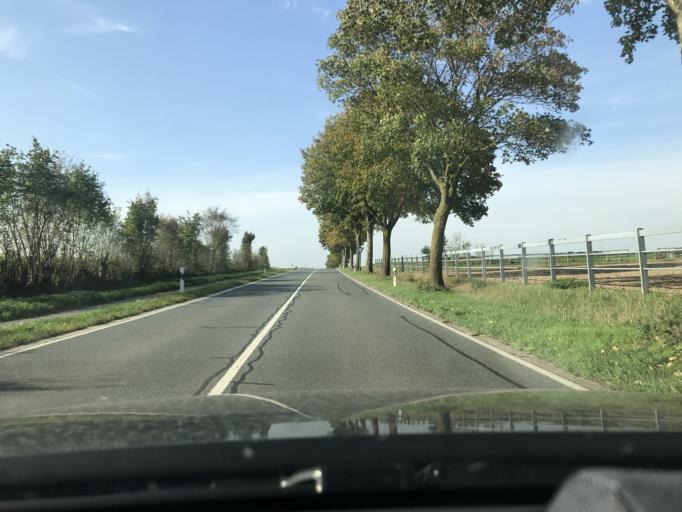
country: DE
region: North Rhine-Westphalia
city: Kalkar
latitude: 51.7357
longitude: 6.2568
